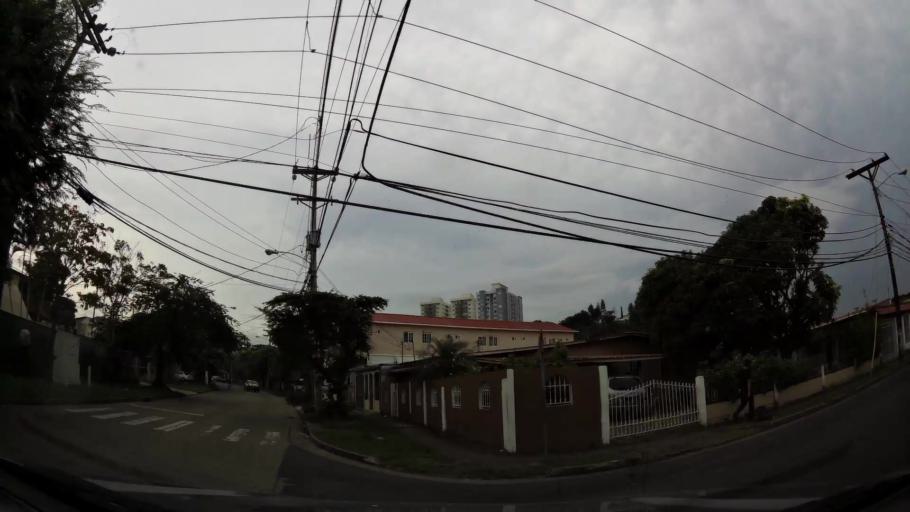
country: PA
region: Panama
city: Panama
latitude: 9.0199
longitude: -79.5271
